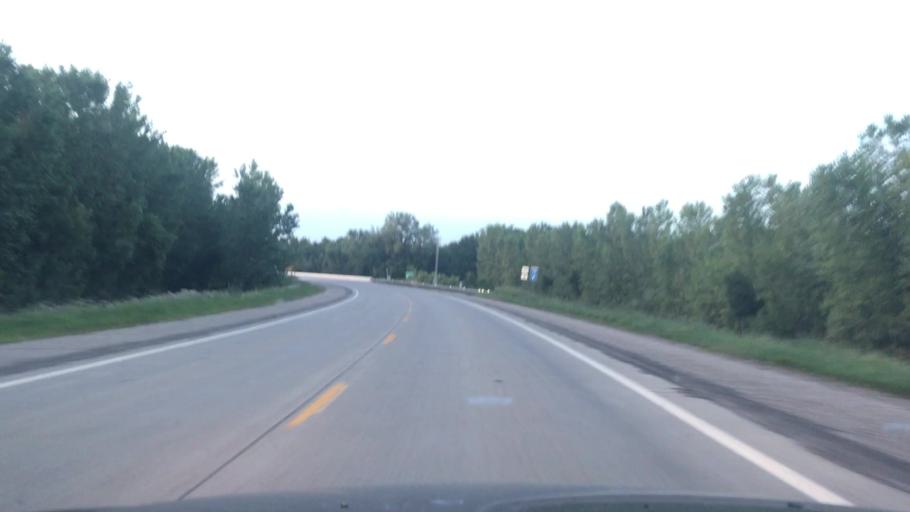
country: US
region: Minnesota
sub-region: Redwood County
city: Redwood Falls
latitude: 44.5437
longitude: -94.9965
